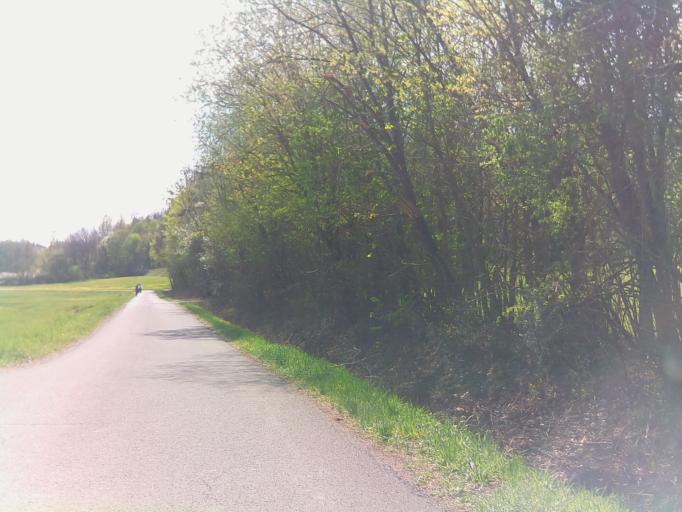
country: DE
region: Bavaria
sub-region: Upper Franconia
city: Weitramsdorf
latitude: 50.2987
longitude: 10.7923
